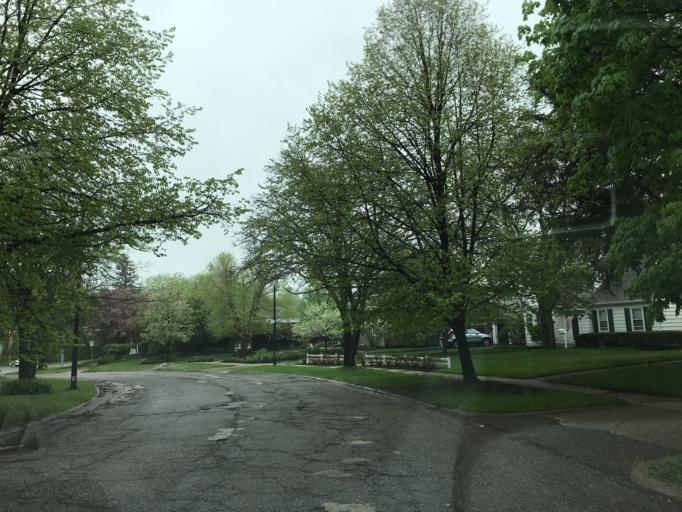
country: US
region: Michigan
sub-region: Washtenaw County
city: Ann Arbor
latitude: 42.2601
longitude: -83.7198
